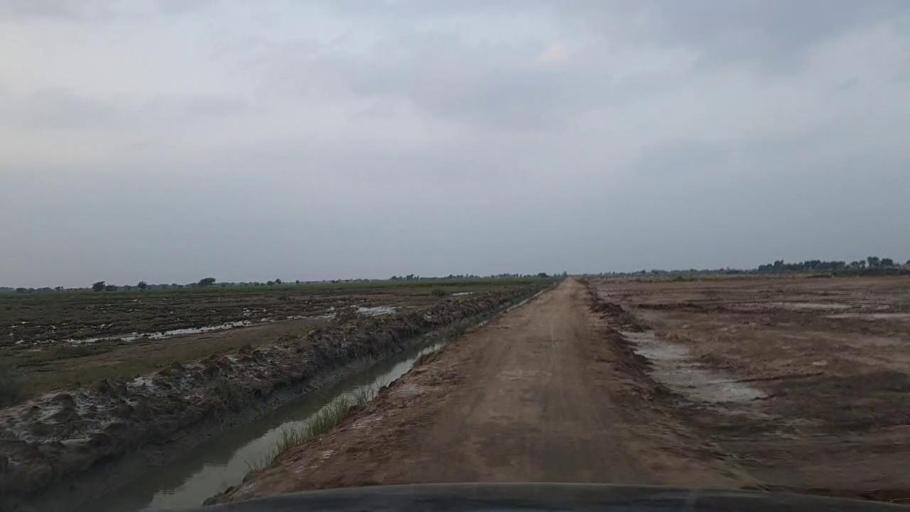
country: PK
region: Sindh
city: Jati
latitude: 24.4991
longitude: 68.3932
